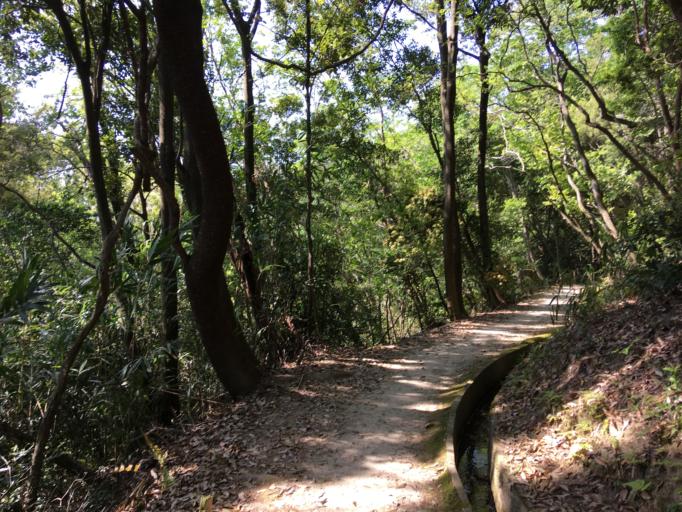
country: JP
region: Nara
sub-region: Ikoma-shi
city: Ikoma
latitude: 34.6996
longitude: 135.7121
